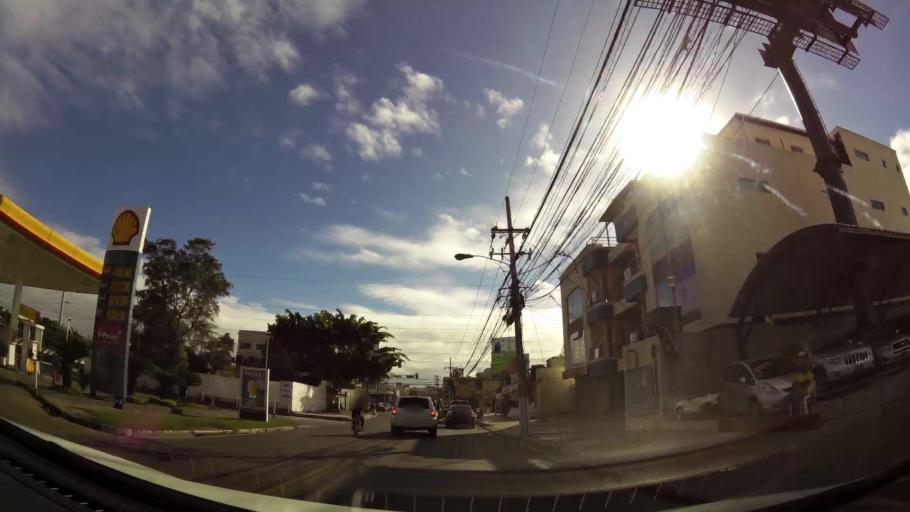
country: DO
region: Nacional
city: Bella Vista
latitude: 18.4671
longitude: -69.9520
